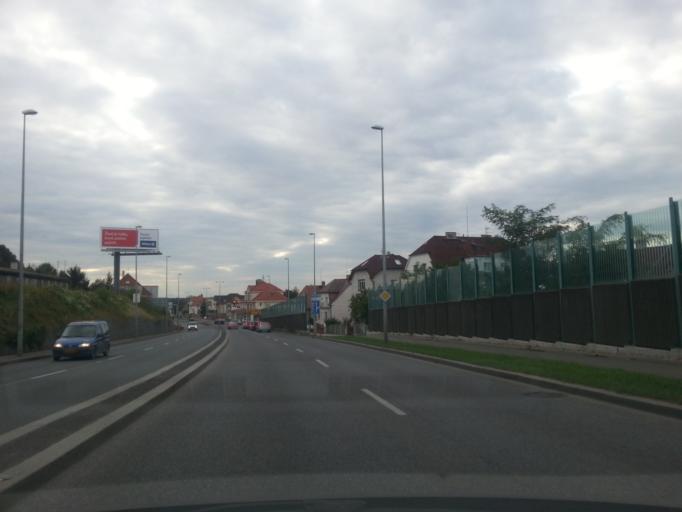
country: CZ
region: Central Bohemia
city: Hostivice
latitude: 50.0769
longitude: 14.3065
